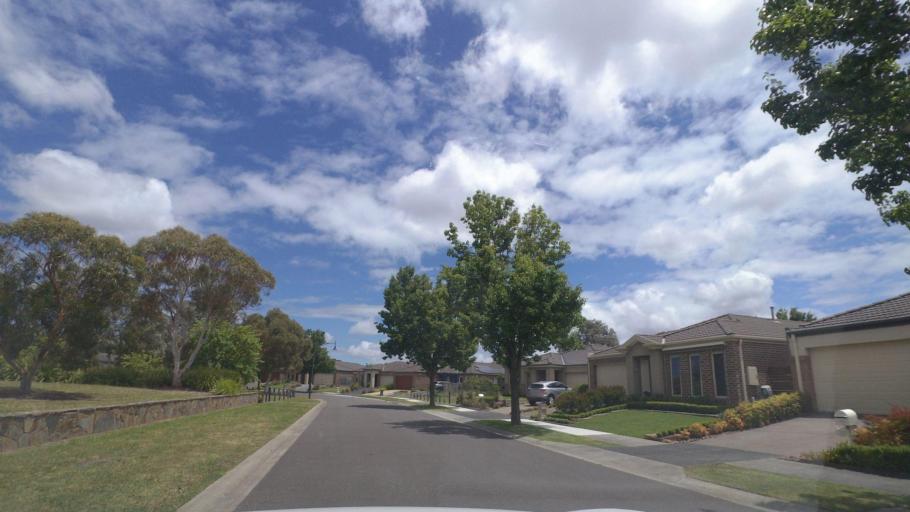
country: AU
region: Victoria
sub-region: Knox
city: Ferntree Gully
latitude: -37.9021
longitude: 145.2773
